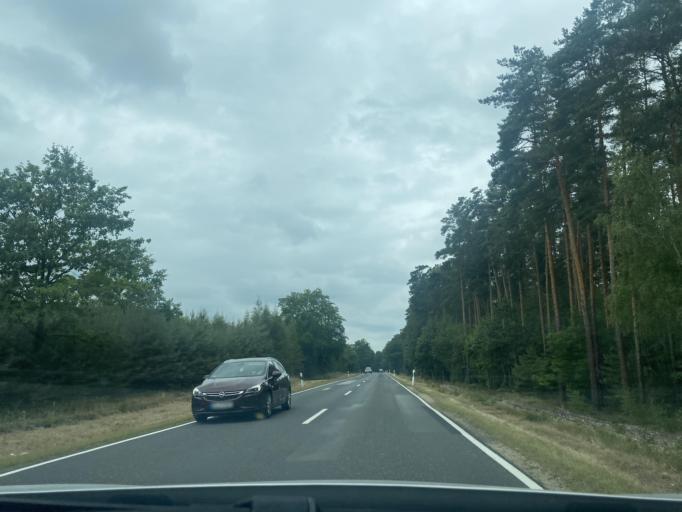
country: DE
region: Saxony
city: Mucka
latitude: 51.2850
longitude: 14.7222
